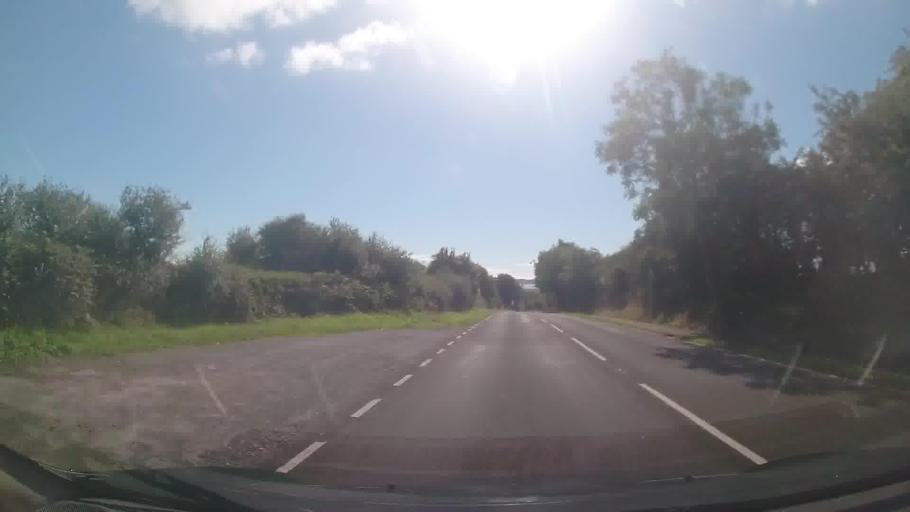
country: GB
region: Wales
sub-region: Pembrokeshire
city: Penally
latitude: 51.6662
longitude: -4.7225
